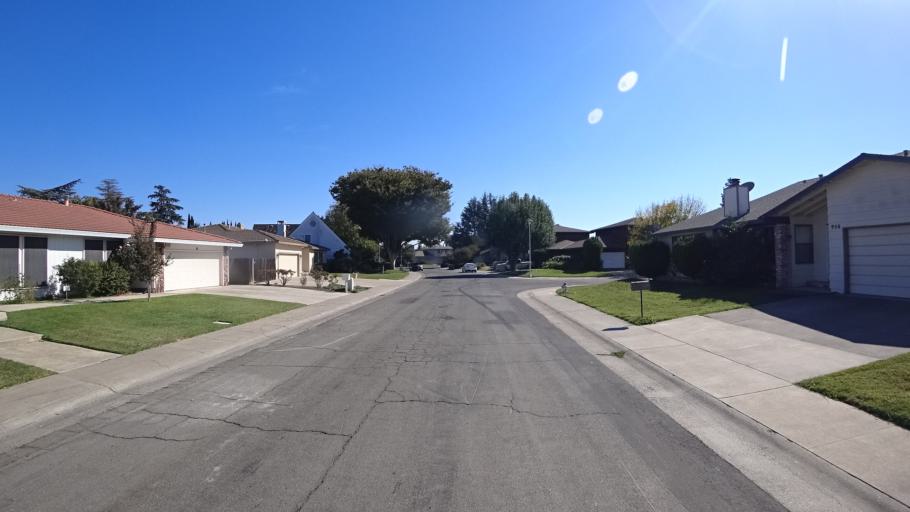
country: US
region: California
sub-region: Sacramento County
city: Parkway
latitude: 38.4997
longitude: -121.5246
